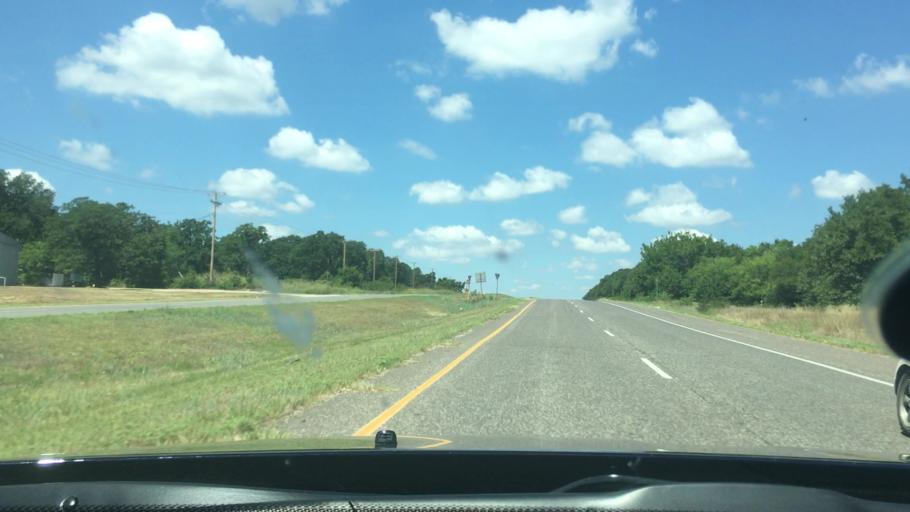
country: US
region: Oklahoma
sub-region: Carter County
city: Lone Grove
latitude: 34.1731
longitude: -97.2900
